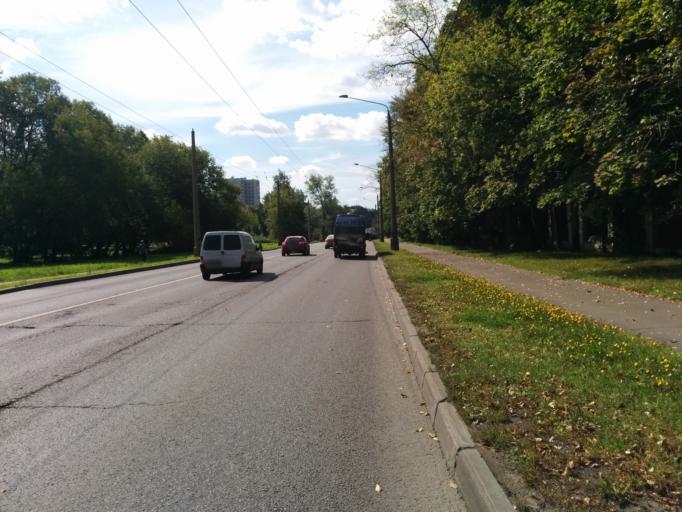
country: RU
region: Moscow
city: Ostankinskiy
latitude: 55.8161
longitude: 37.6177
